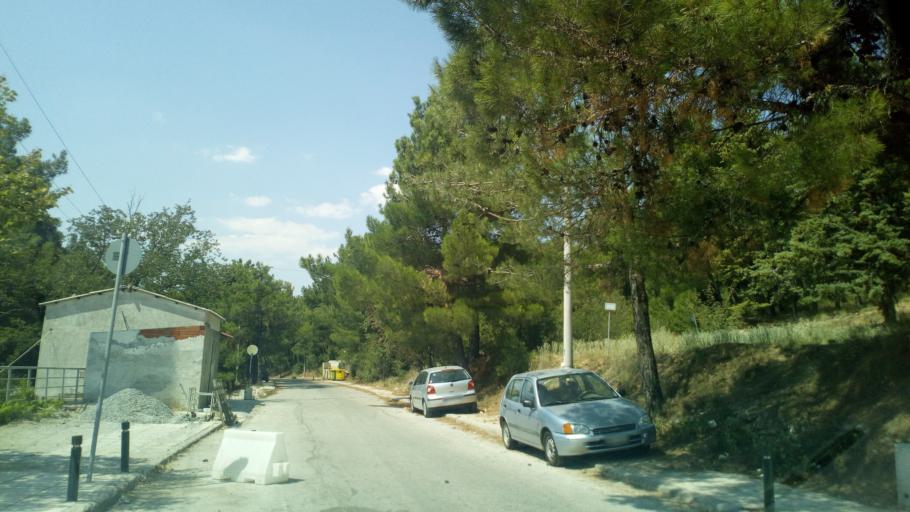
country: GR
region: Central Macedonia
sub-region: Nomos Thessalonikis
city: Asvestochori
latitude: 40.6314
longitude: 23.0468
